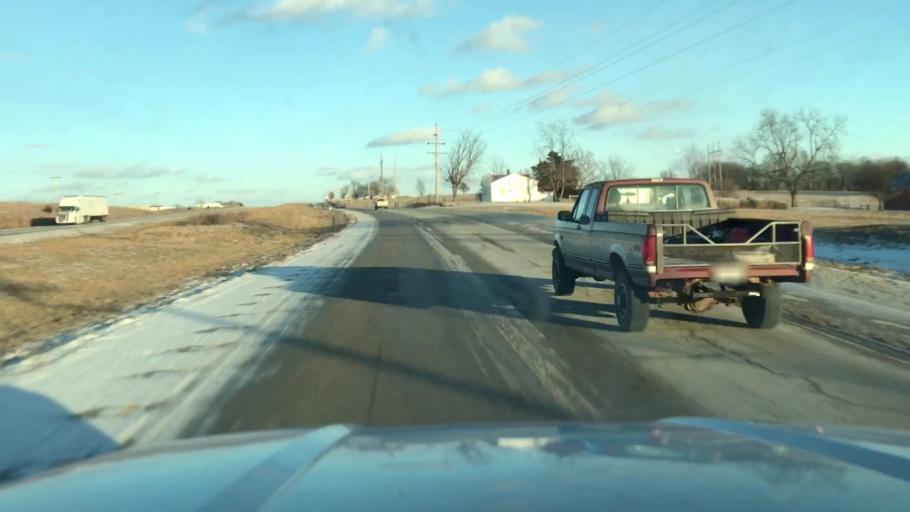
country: US
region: Missouri
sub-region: Clinton County
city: Cameron
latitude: 39.7548
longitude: -94.3110
